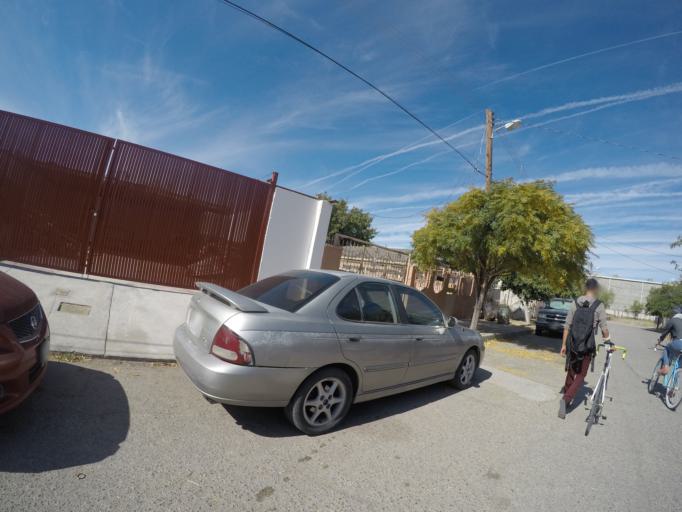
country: MX
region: Chihuahua
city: Ciudad Juarez
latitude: 31.7339
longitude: -106.4444
